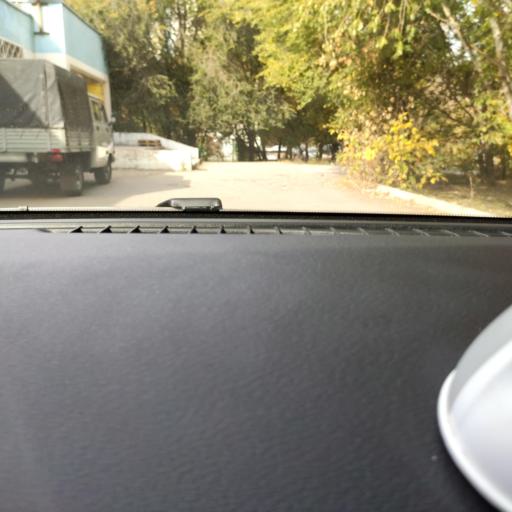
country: RU
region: Samara
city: Samara
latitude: 53.2003
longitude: 50.1448
